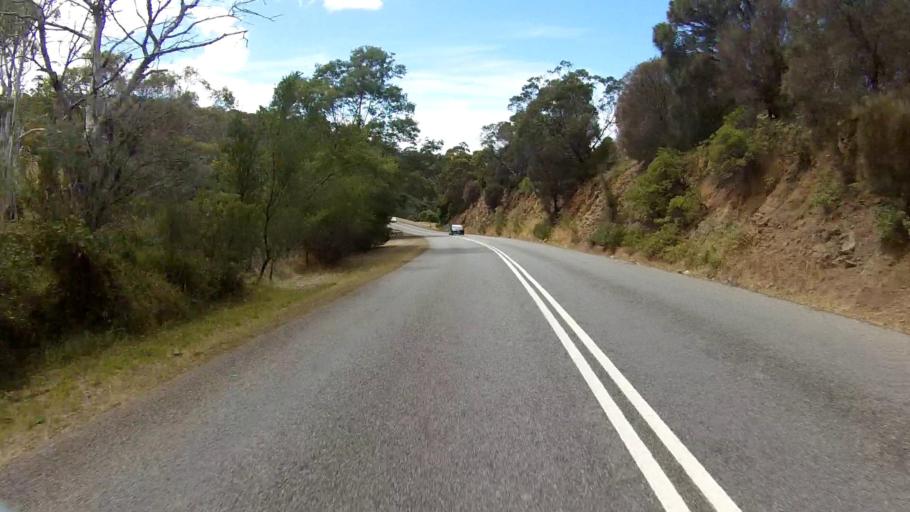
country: AU
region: Tasmania
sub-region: Sorell
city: Sorell
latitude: -42.2292
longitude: 148.0229
